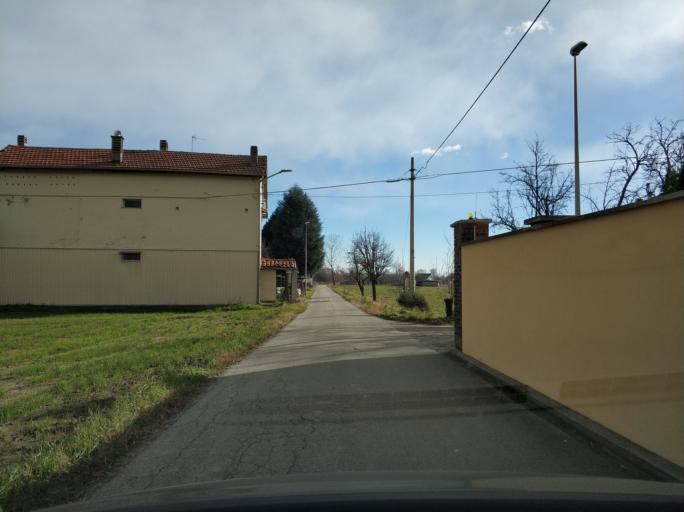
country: IT
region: Piedmont
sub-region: Provincia di Torino
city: Robassomero
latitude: 45.2179
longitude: 7.5753
